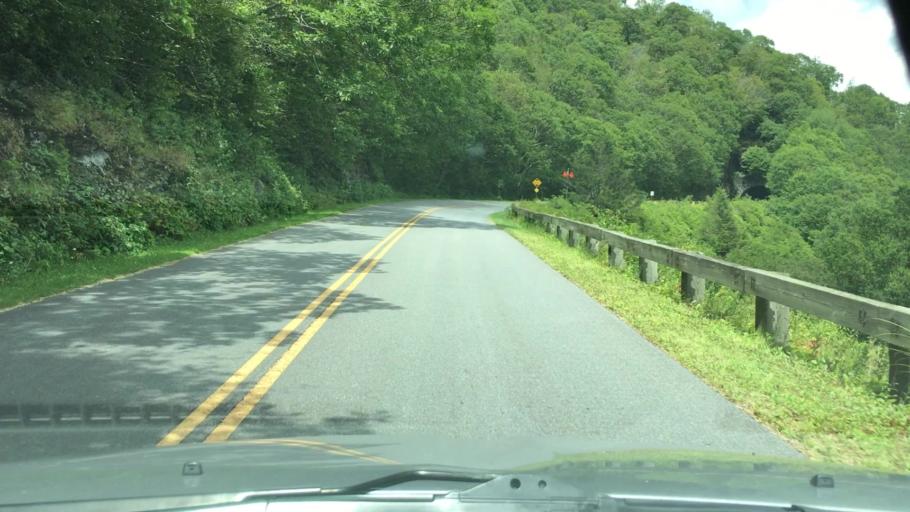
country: US
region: North Carolina
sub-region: Buncombe County
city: Swannanoa
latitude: 35.6850
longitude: -82.3851
